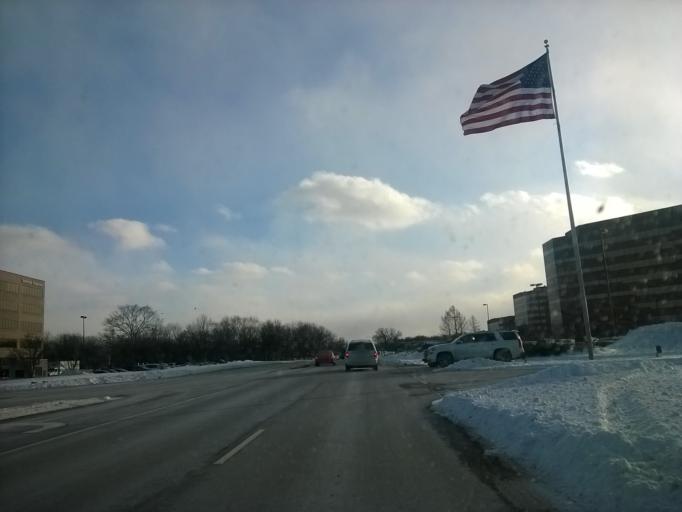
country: US
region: Indiana
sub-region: Hamilton County
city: Carmel
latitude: 39.9585
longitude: -86.1552
